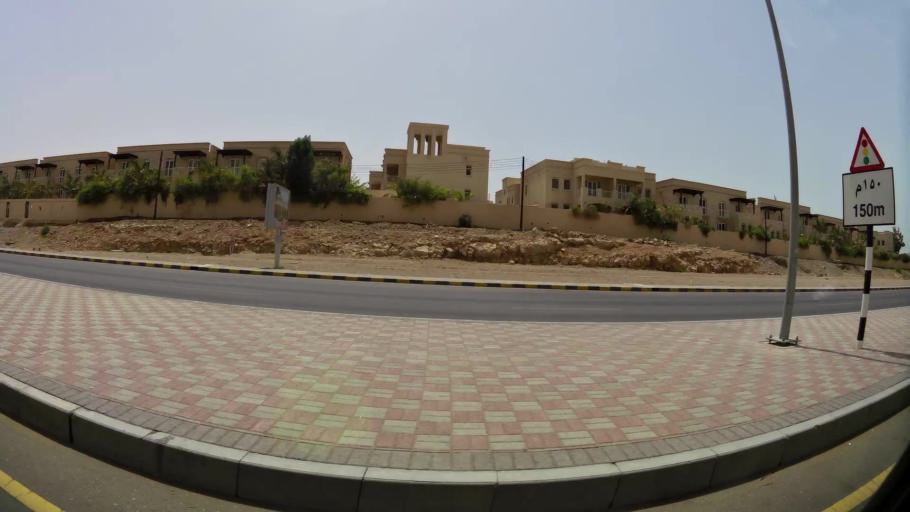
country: OM
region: Muhafazat Masqat
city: Bawshar
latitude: 23.5597
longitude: 58.4022
